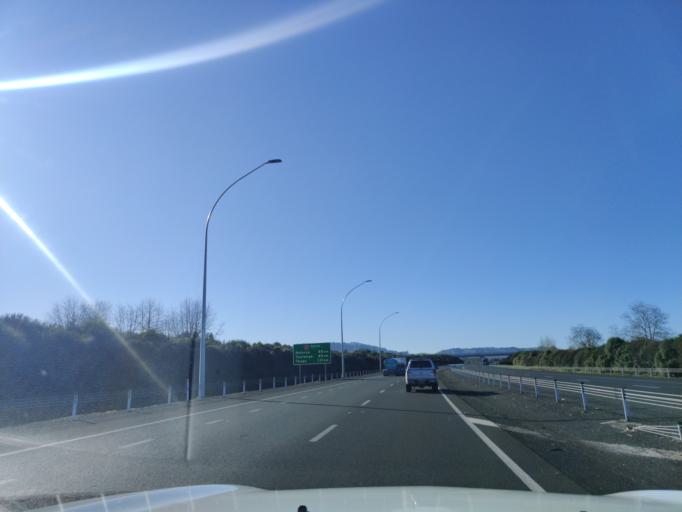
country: NZ
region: Waikato
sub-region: Waipa District
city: Cambridge
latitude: -37.8683
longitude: 175.4670
